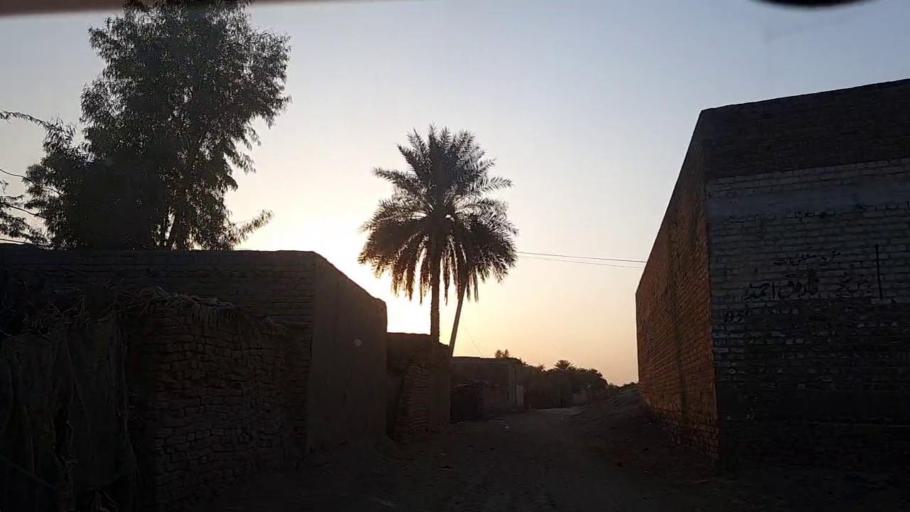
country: PK
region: Sindh
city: Shikarpur
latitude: 27.9599
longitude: 68.6218
